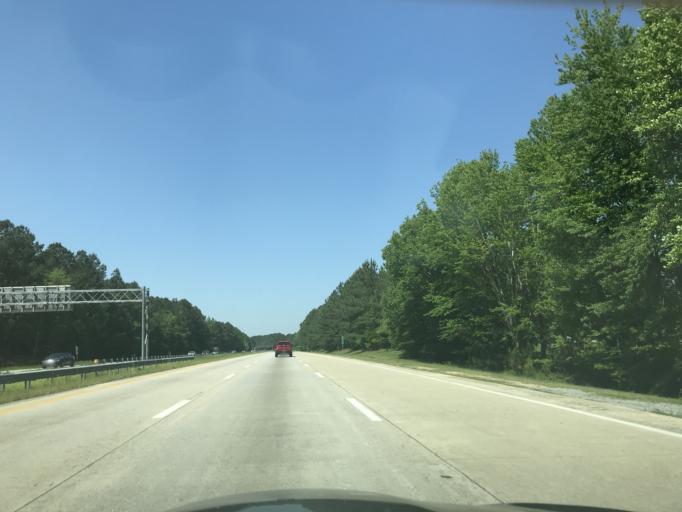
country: US
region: North Carolina
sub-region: Johnston County
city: Benson
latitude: 35.4423
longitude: -78.5343
